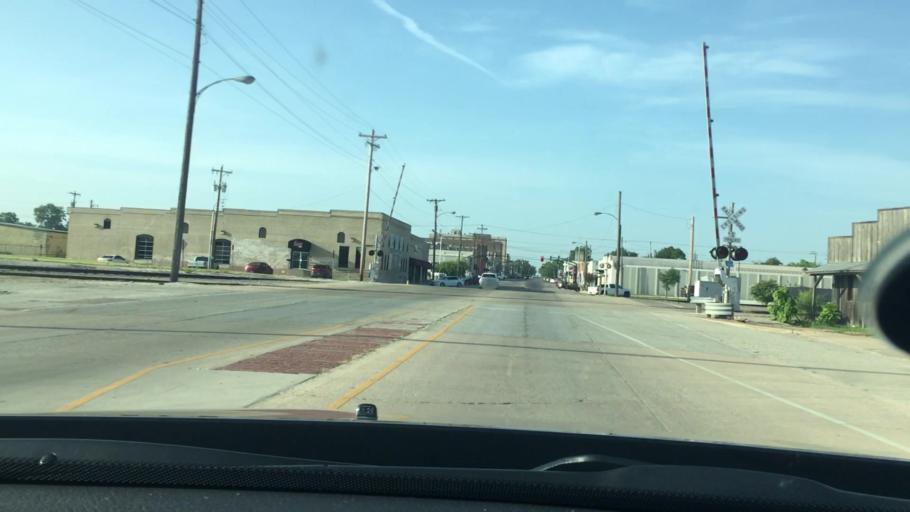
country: US
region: Oklahoma
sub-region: Pontotoc County
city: Ada
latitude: 34.7774
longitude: -96.6787
